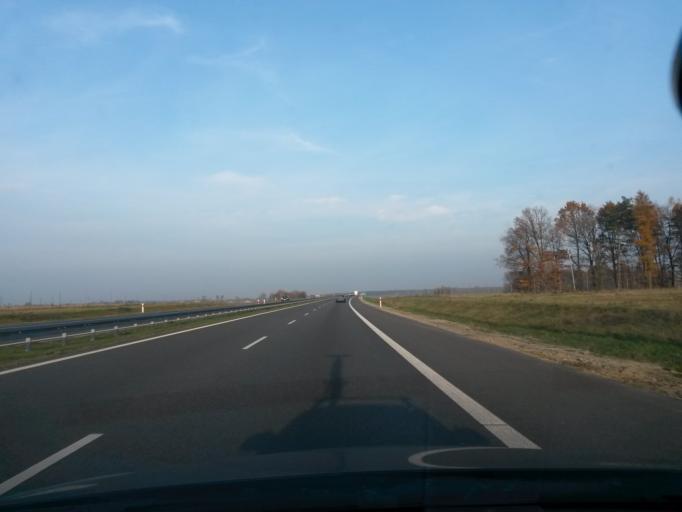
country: PL
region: Lower Silesian Voivodeship
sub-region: Powiat olesnicki
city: Twardogora
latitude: 51.2749
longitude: 17.5593
